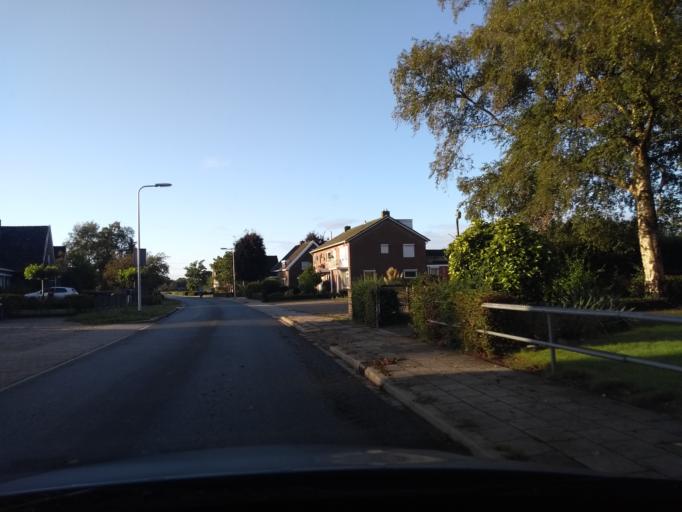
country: NL
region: Overijssel
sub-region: Gemeente Raalte
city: Raalte
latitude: 52.3588
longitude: 6.3839
